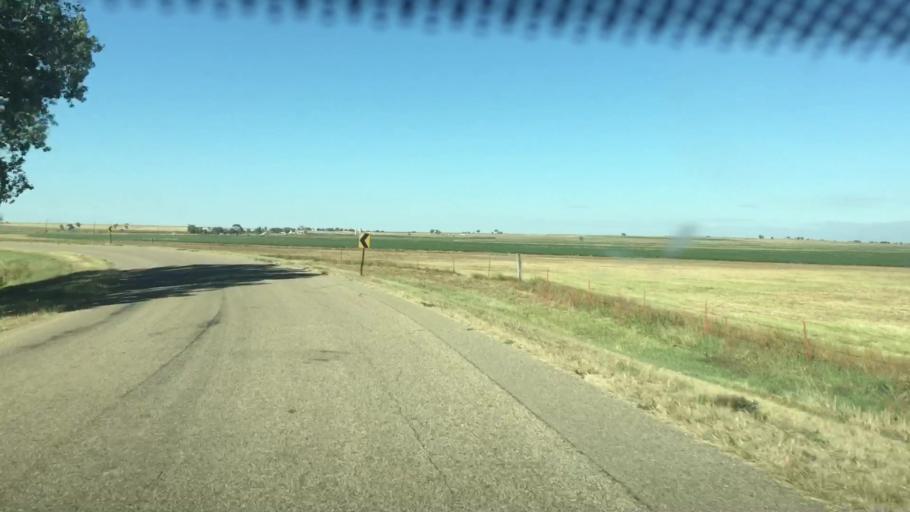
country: US
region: Colorado
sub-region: Prowers County
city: Lamar
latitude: 38.0981
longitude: -102.5194
